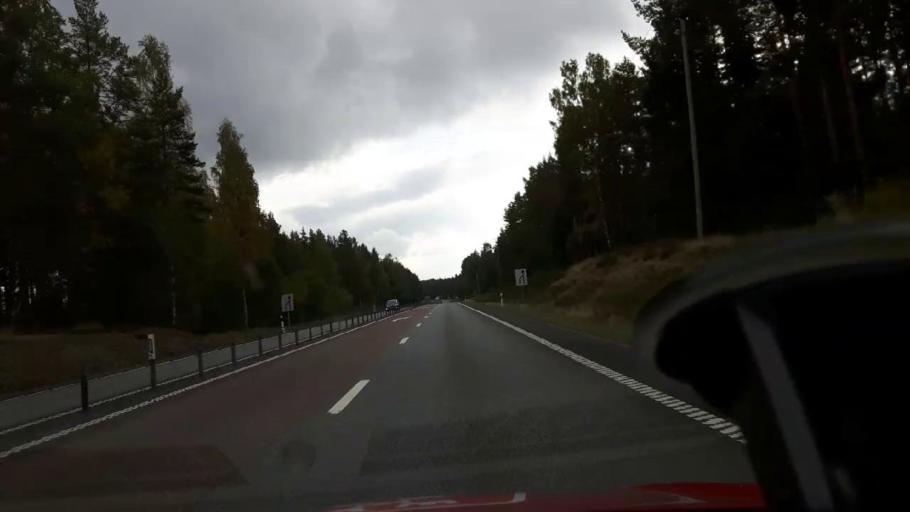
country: SE
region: Gaevleborg
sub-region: Gavle Kommun
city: Norrsundet
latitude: 61.0132
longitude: 16.9808
